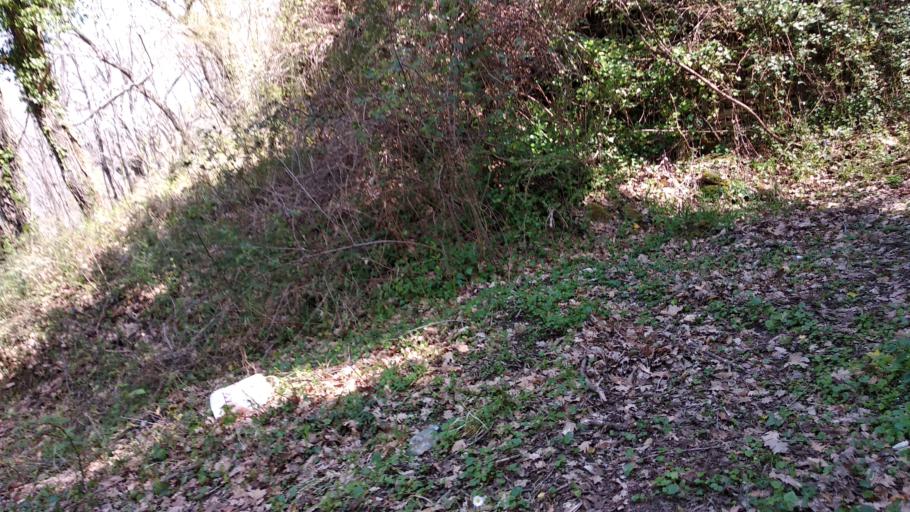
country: IT
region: Calabria
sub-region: Provincia di Cosenza
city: Altilia
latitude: 39.1298
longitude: 16.2494
